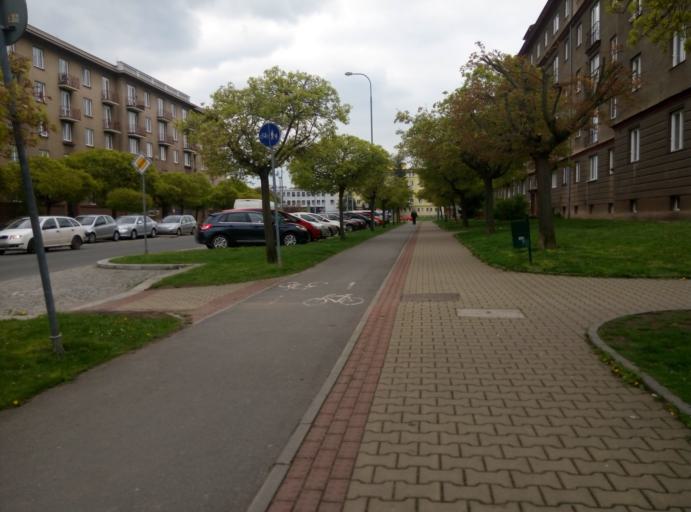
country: CZ
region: Plzensky
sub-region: Okres Plzen-Mesto
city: Pilsen
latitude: 49.7270
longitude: 13.4032
